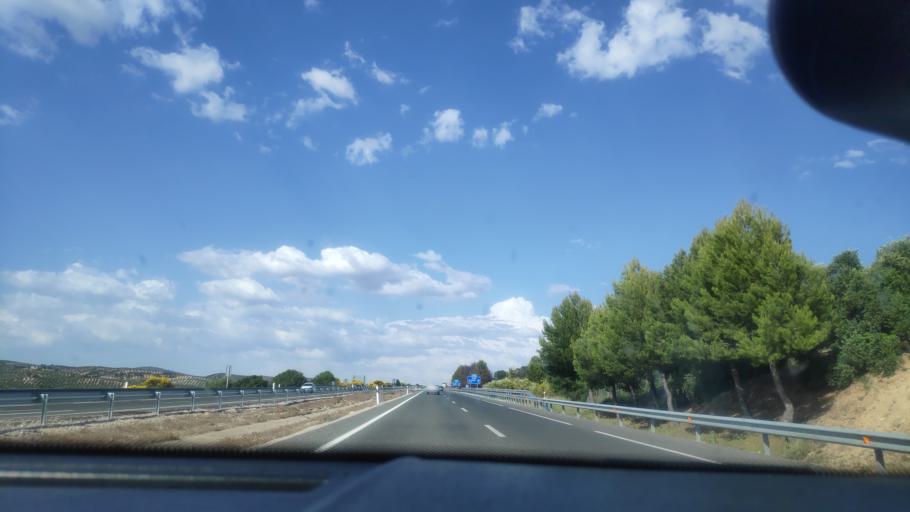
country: ES
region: Andalusia
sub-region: Provincia de Granada
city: Campotejar
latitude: 37.4880
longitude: -3.5947
